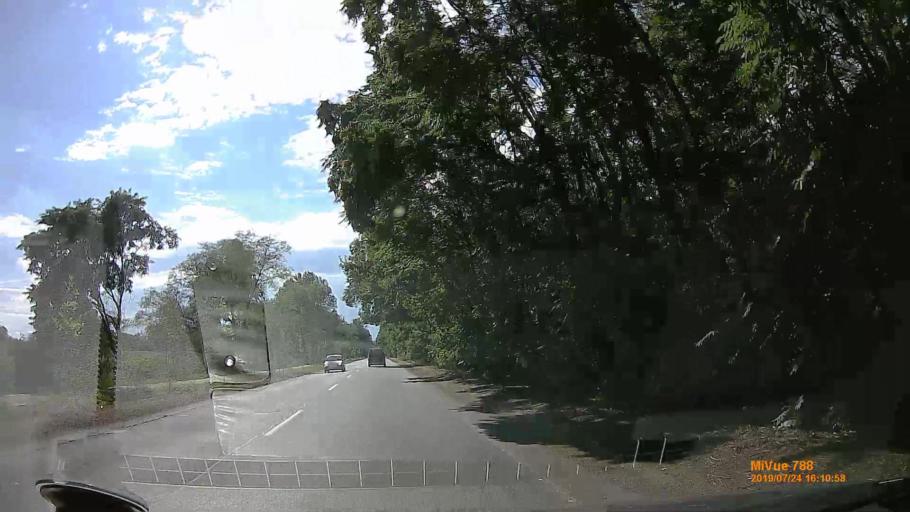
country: HU
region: Szabolcs-Szatmar-Bereg
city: Napkor
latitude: 47.9500
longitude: 21.8412
